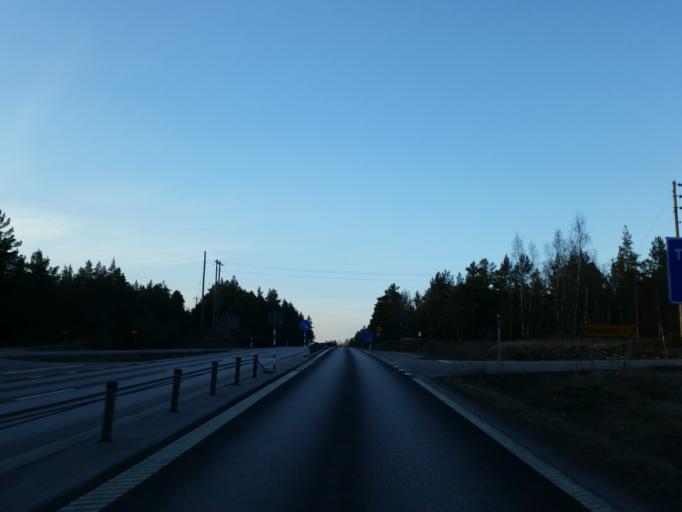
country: SE
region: Kalmar
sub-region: Oskarshamns Kommun
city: Oskarshamn
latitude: 57.3629
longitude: 16.4944
